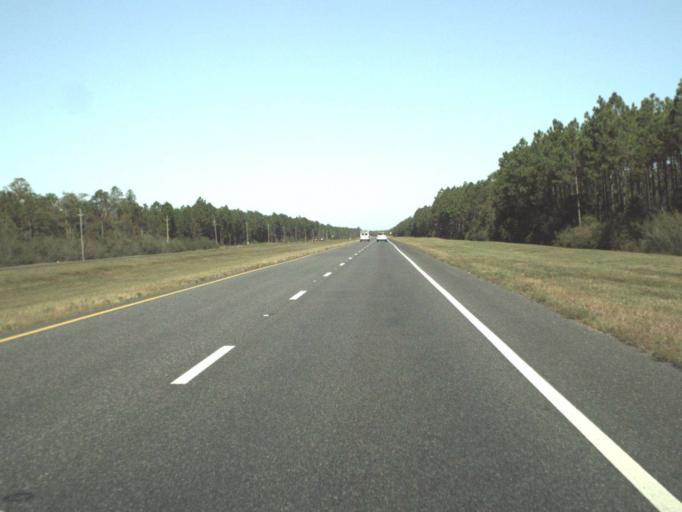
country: US
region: Florida
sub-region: Walton County
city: Seaside
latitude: 30.3103
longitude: -86.0369
